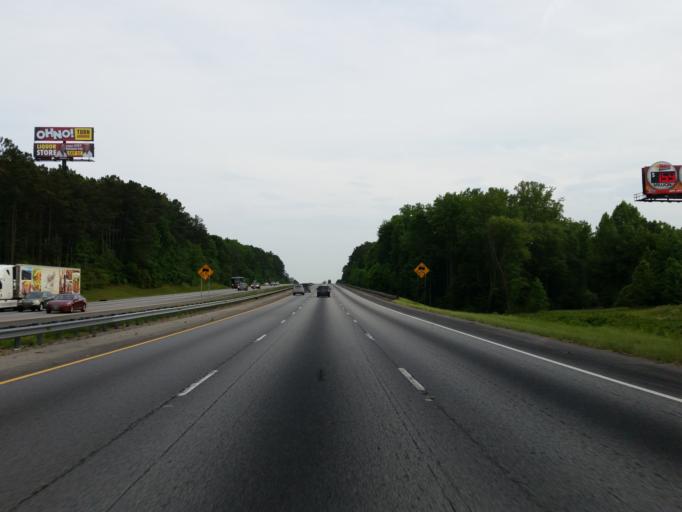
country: US
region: Georgia
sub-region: Henry County
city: Locust Grove
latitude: 33.3416
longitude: -84.1235
